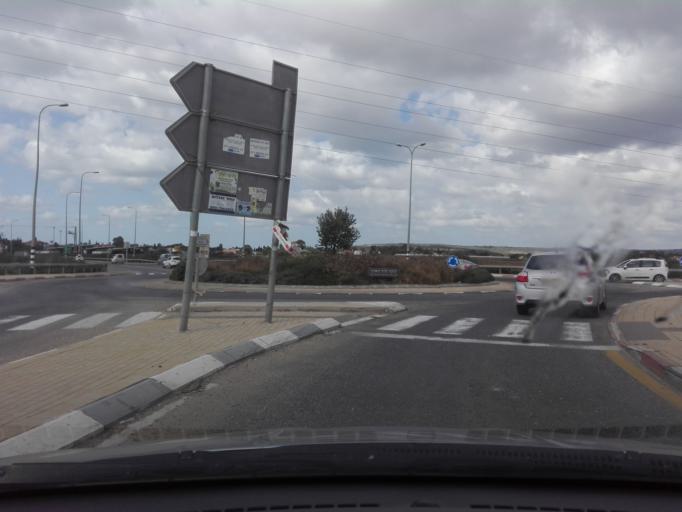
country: IL
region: Haifa
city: Qesarya
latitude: 32.5105
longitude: 34.9575
